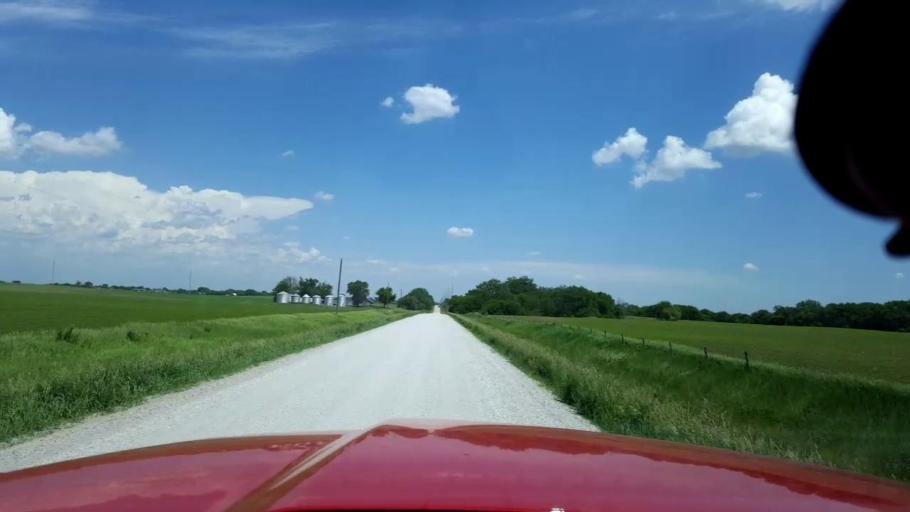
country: US
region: Iowa
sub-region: Boone County
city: Boone
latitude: 42.0493
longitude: -93.7650
